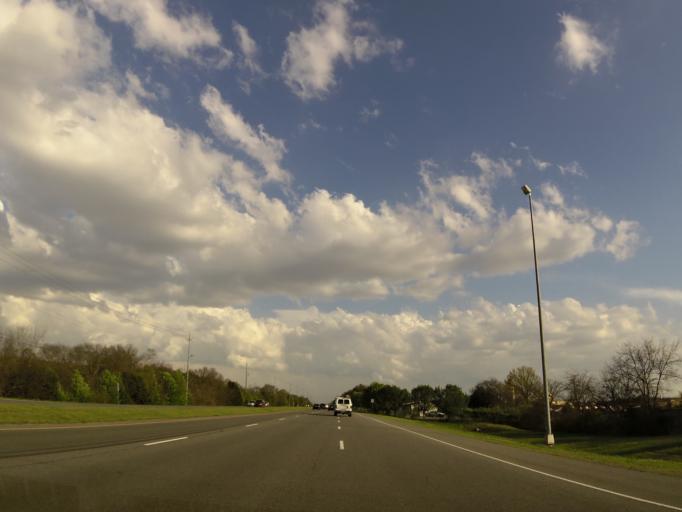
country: US
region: Tennessee
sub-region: Rutherford County
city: Murfreesboro
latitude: 35.8974
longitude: -86.4445
